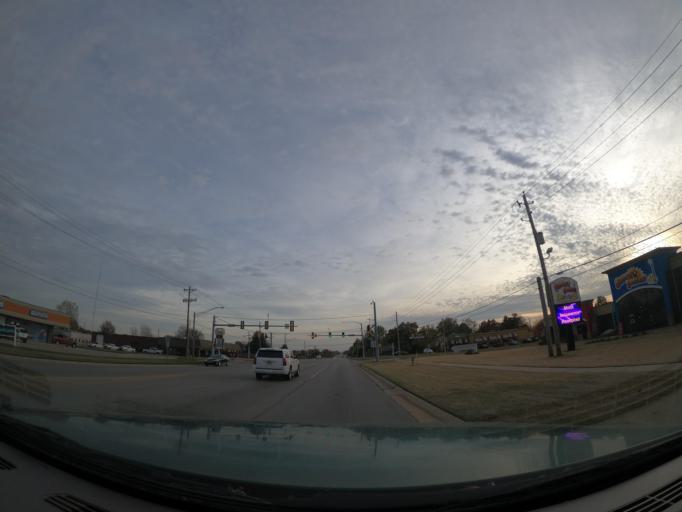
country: US
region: Oklahoma
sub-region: Tulsa County
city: Broken Arrow
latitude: 36.0548
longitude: -95.8154
